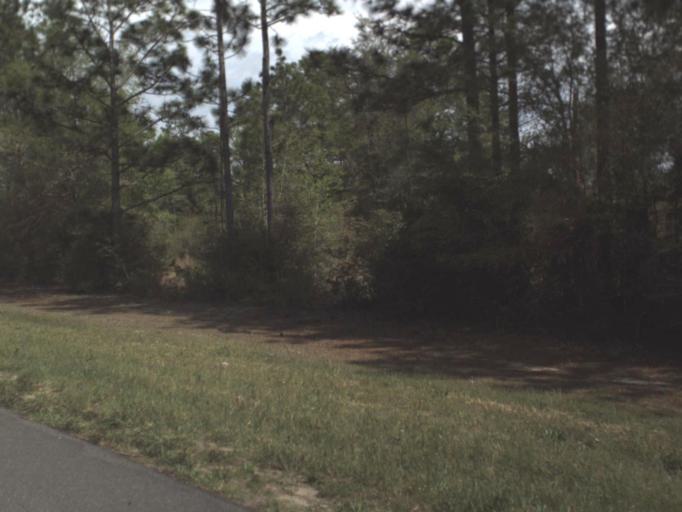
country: US
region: Florida
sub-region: Santa Rosa County
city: East Milton
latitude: 30.6502
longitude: -86.9050
